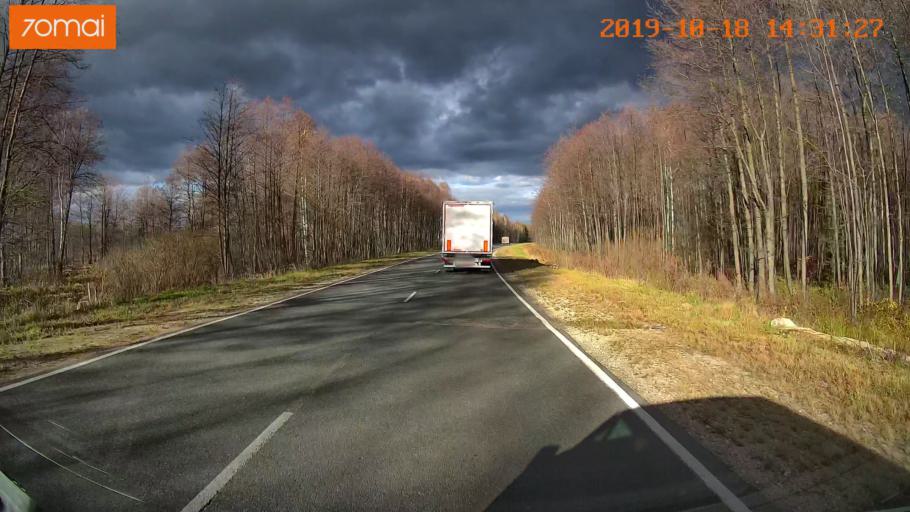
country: RU
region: Rjazan
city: Tuma
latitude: 55.1827
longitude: 40.5701
